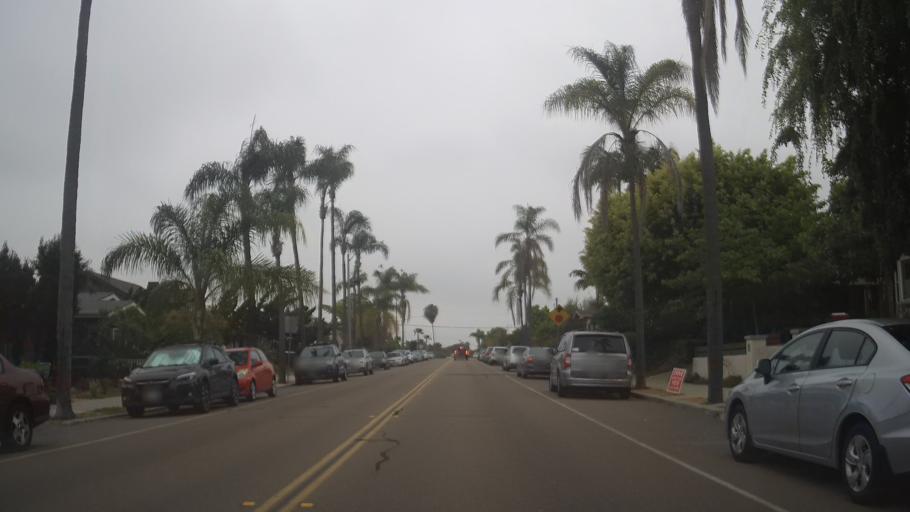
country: US
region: California
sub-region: San Diego County
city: San Diego
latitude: 32.7442
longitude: -117.1390
